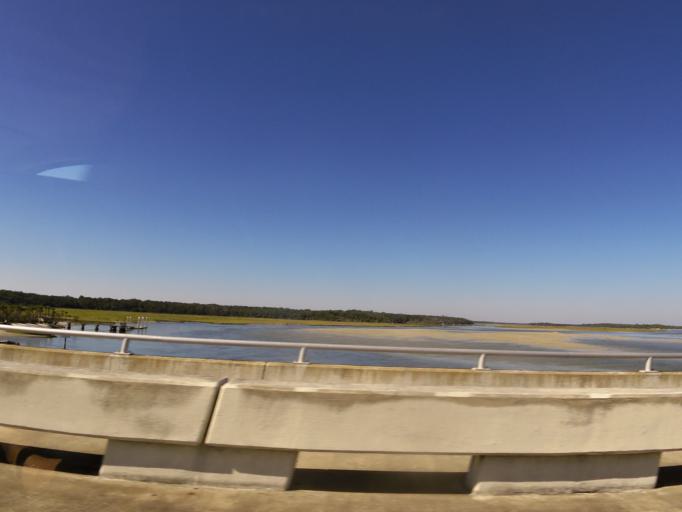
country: US
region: Florida
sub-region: Duval County
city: Atlantic Beach
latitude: 30.4200
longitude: -81.4186
